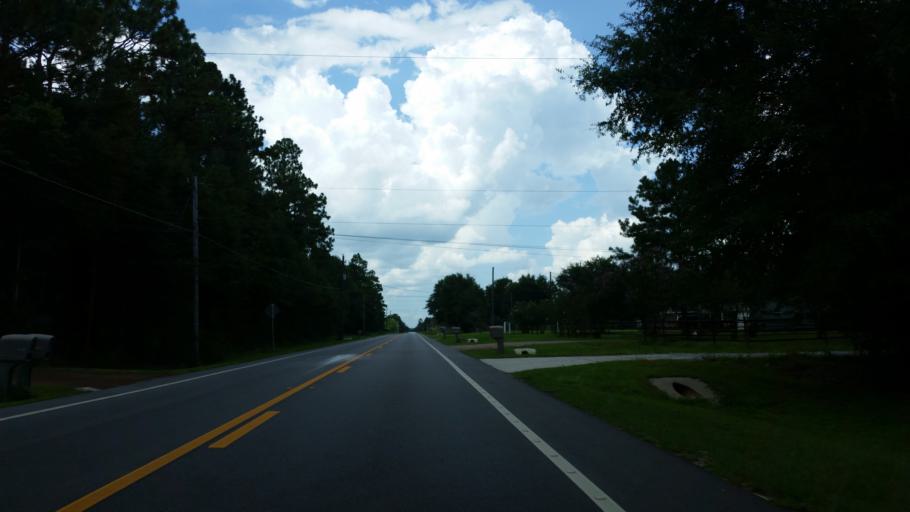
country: US
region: Florida
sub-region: Escambia County
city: Cantonment
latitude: 30.6433
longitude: -87.3859
